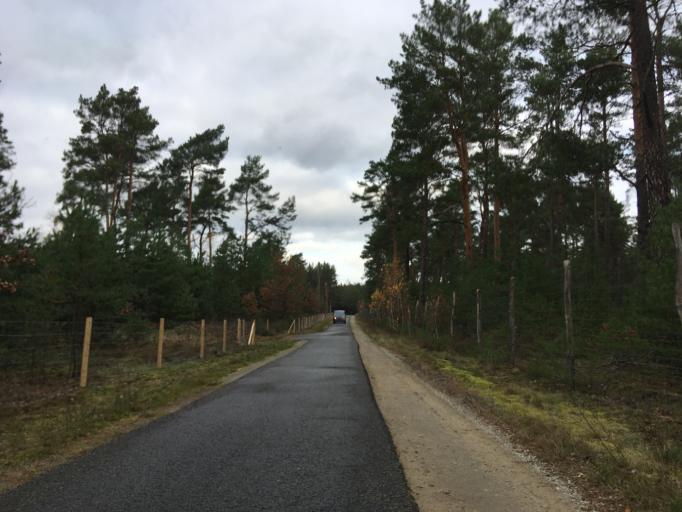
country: DE
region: Brandenburg
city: Tauer
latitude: 51.9920
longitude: 14.5156
